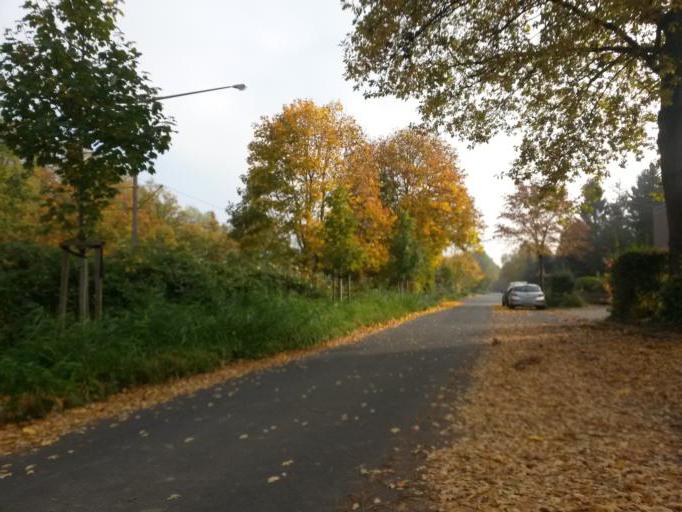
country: DE
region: Bremen
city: Bremen
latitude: 53.0809
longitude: 8.8567
